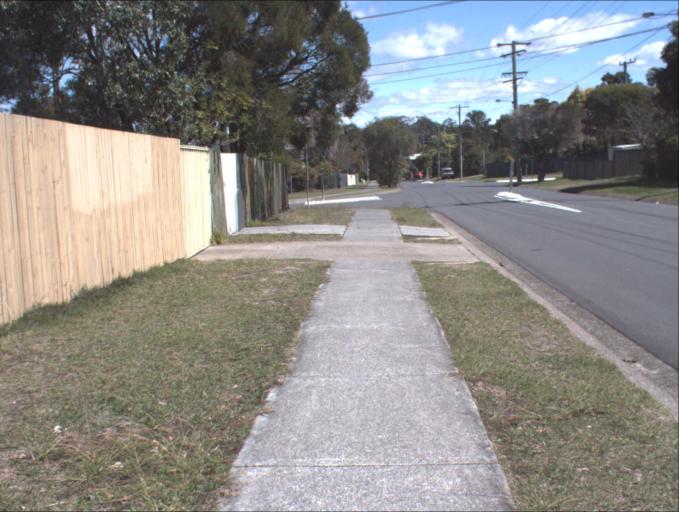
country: AU
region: Queensland
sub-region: Logan
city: Waterford West
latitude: -27.6881
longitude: 153.0969
